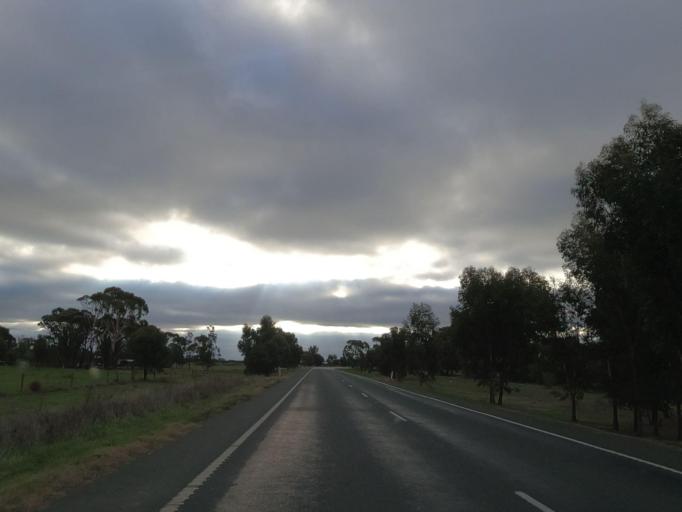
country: AU
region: Victoria
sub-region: Swan Hill
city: Swan Hill
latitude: -35.7310
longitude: 143.8948
